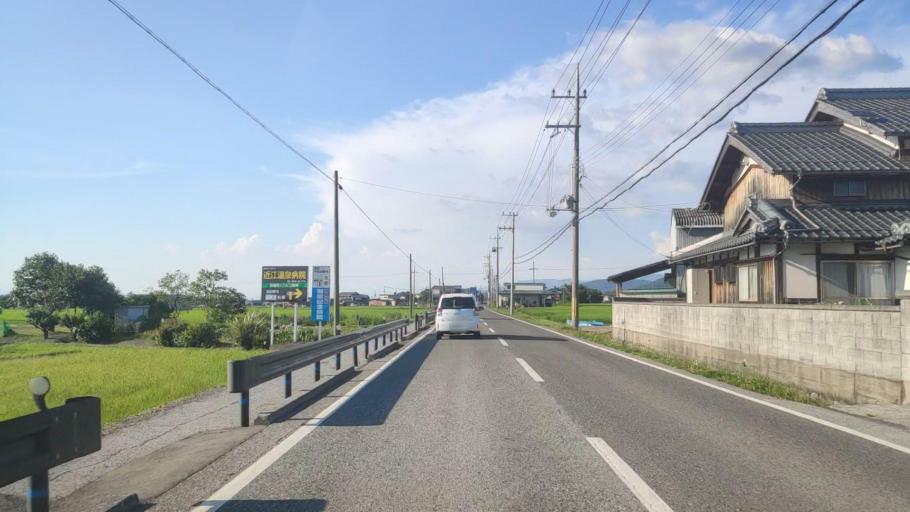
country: JP
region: Shiga Prefecture
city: Youkaichi
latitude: 35.1315
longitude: 136.2609
